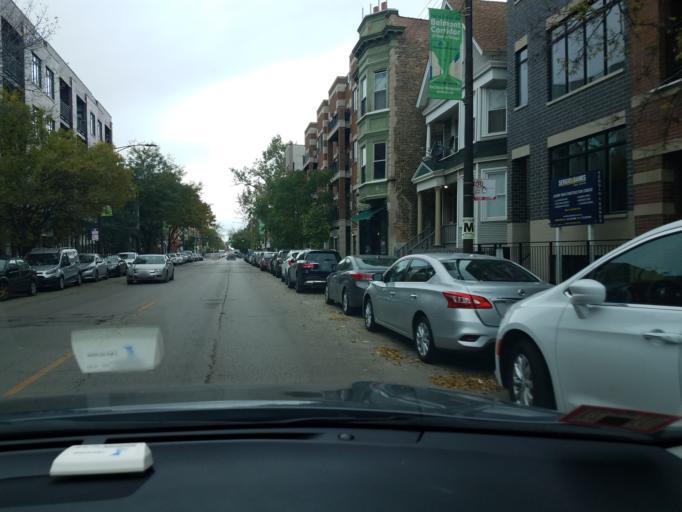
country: US
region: Illinois
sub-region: Cook County
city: Lincolnwood
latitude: 41.9396
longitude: -87.6813
